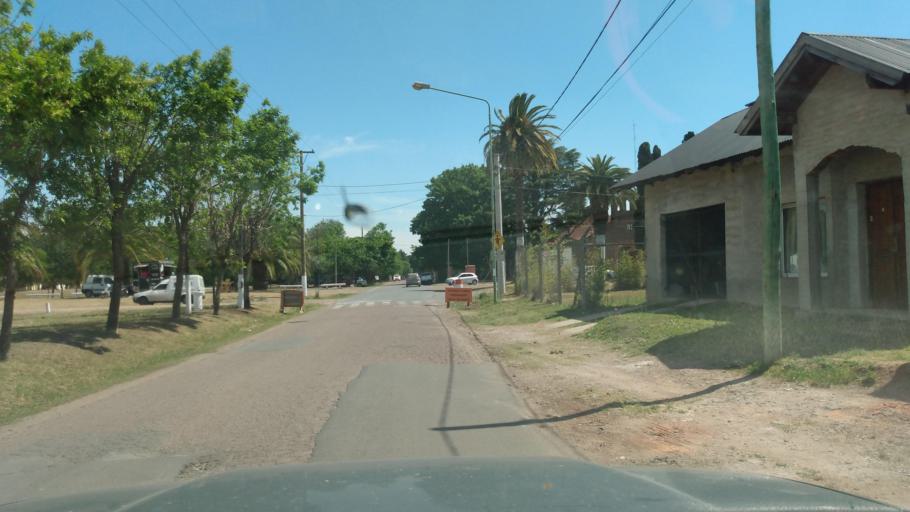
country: AR
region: Buenos Aires
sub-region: Partido de Lujan
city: Lujan
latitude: -34.5998
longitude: -59.1735
